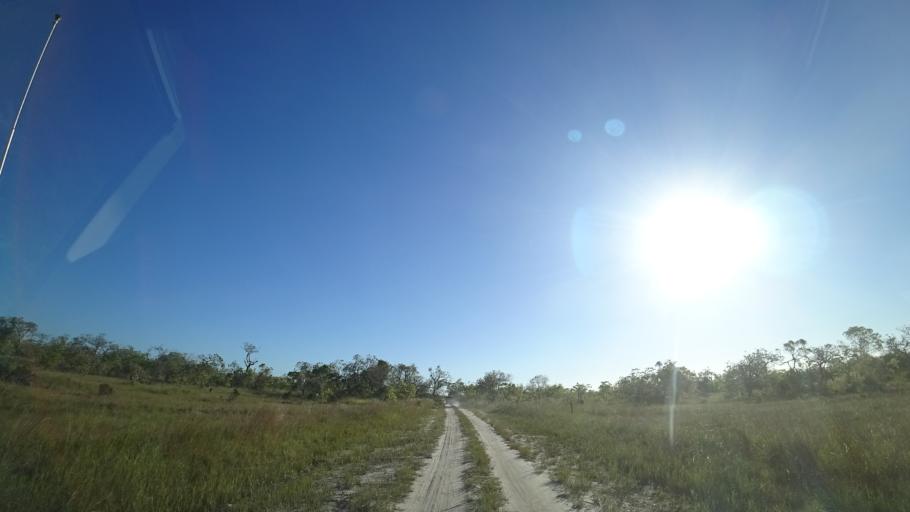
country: MZ
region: Sofala
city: Beira
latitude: -19.5719
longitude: 35.2344
